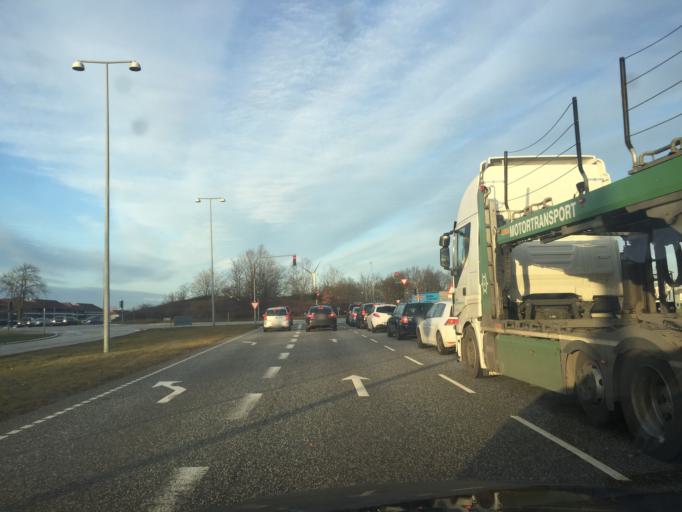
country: DK
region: Capital Region
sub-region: Hoje-Taastrup Kommune
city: Taastrup
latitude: 55.6557
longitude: 12.2829
